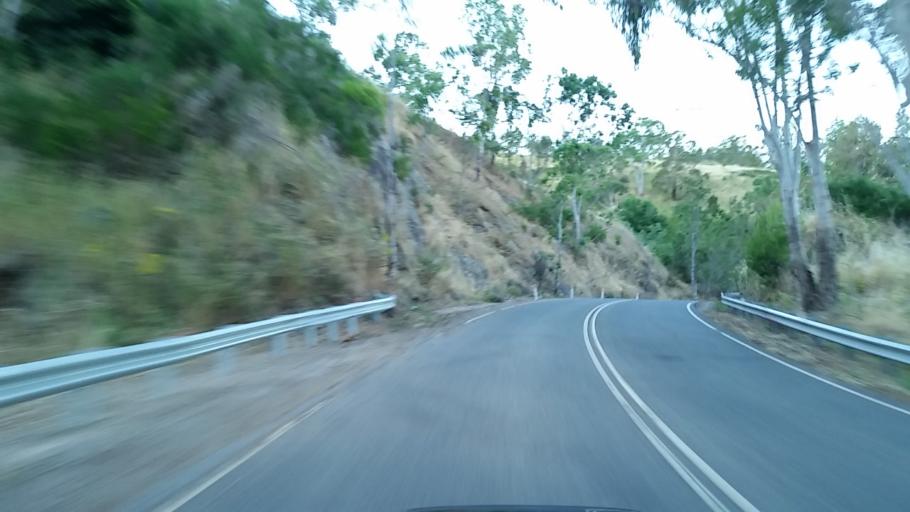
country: AU
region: South Australia
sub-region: Tea Tree Gully
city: Golden Grove
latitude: -34.8515
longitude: 138.7911
